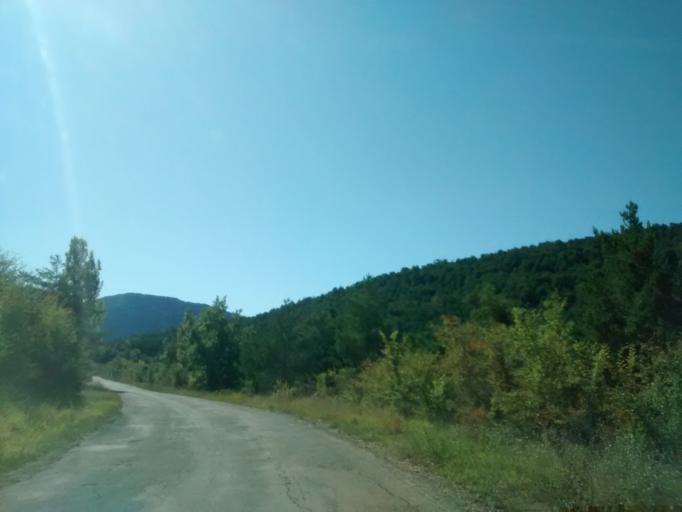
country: ES
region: Aragon
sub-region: Provincia de Huesca
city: Jaca
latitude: 42.5059
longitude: -0.5532
